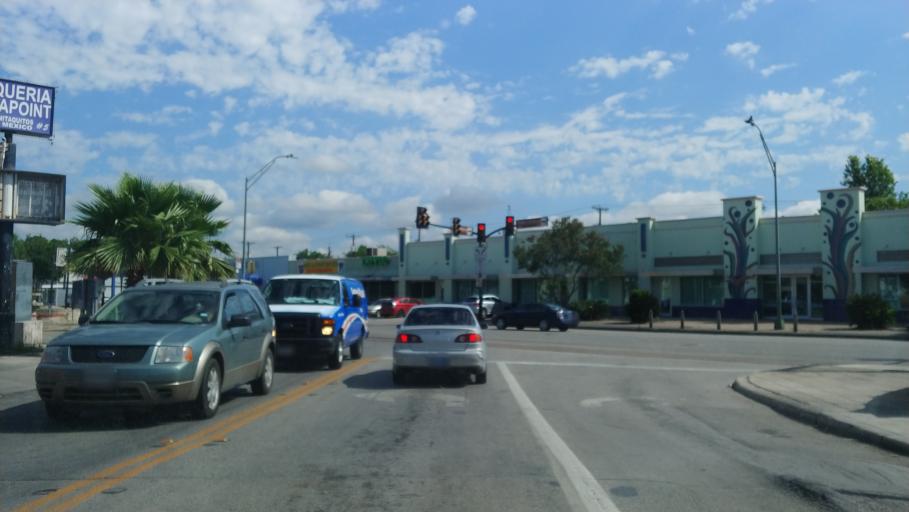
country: US
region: Texas
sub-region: Bexar County
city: Balcones Heights
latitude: 29.4610
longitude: -98.5229
